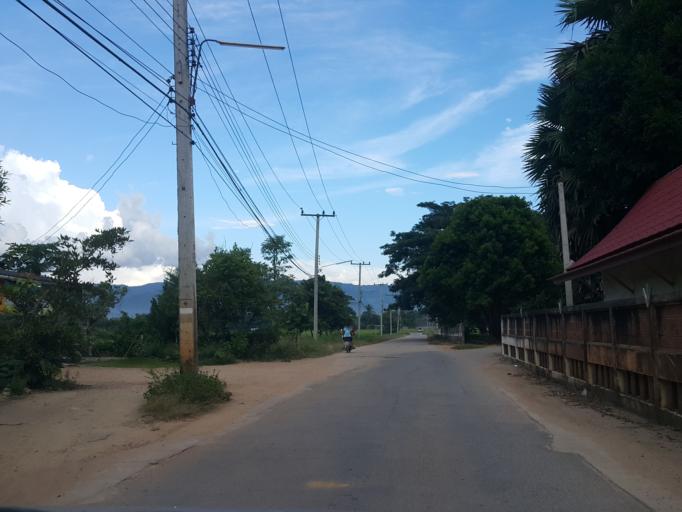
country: TH
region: Chiang Mai
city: Phrao
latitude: 19.3366
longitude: 99.1872
